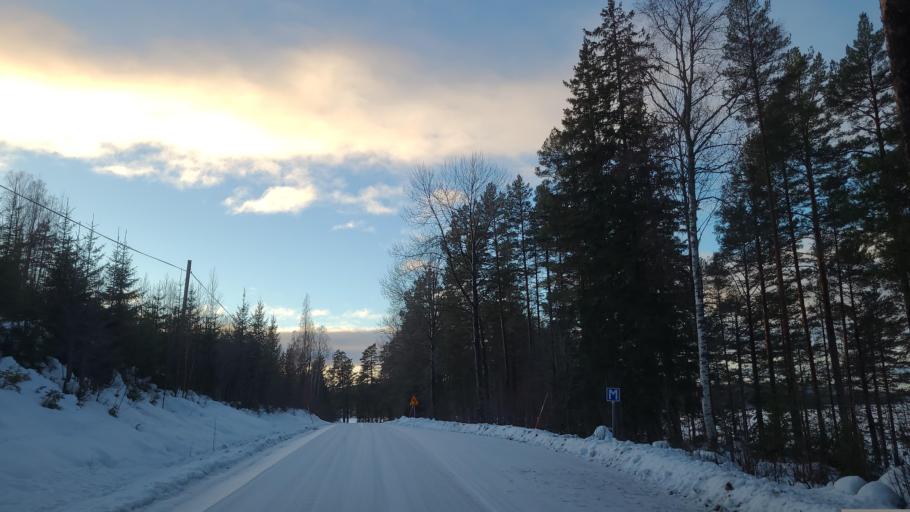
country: SE
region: Gaevleborg
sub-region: Bollnas Kommun
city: Kilafors
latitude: 61.3910
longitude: 16.6874
